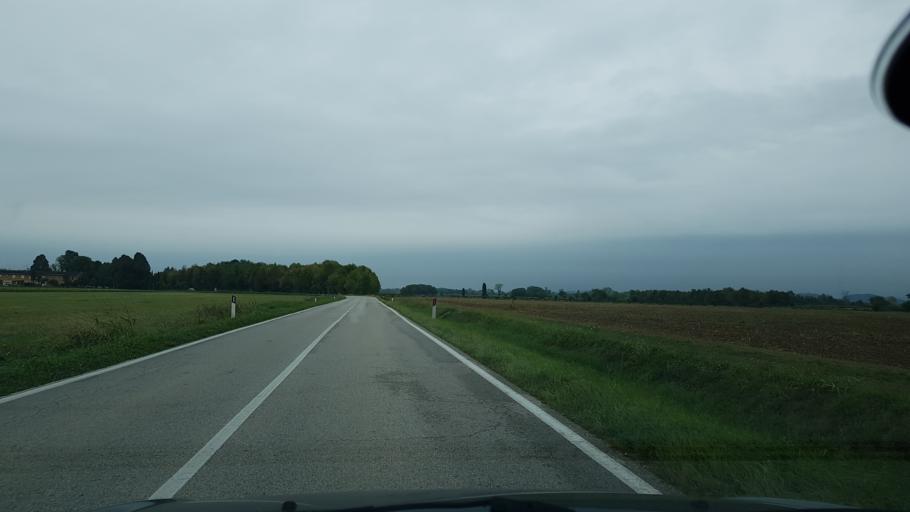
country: IT
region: Friuli Venezia Giulia
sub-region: Provincia di Udine
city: Trivignano Udinese
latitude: 45.9452
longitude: 13.3473
